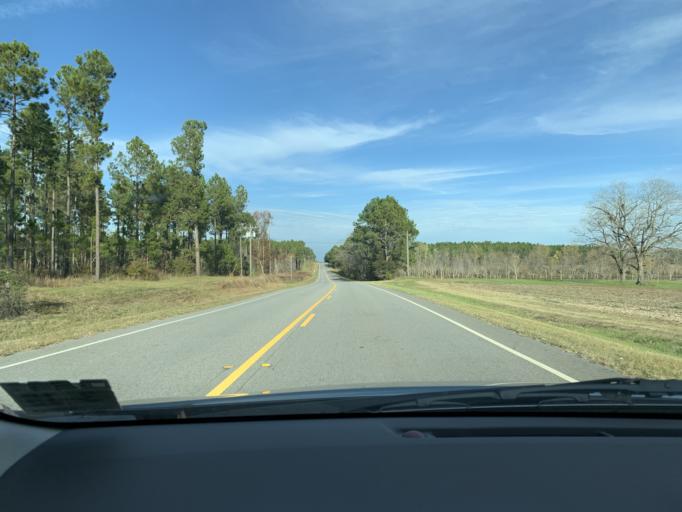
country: US
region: Georgia
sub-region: Tift County
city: Tifton
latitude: 31.5980
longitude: -83.4668
